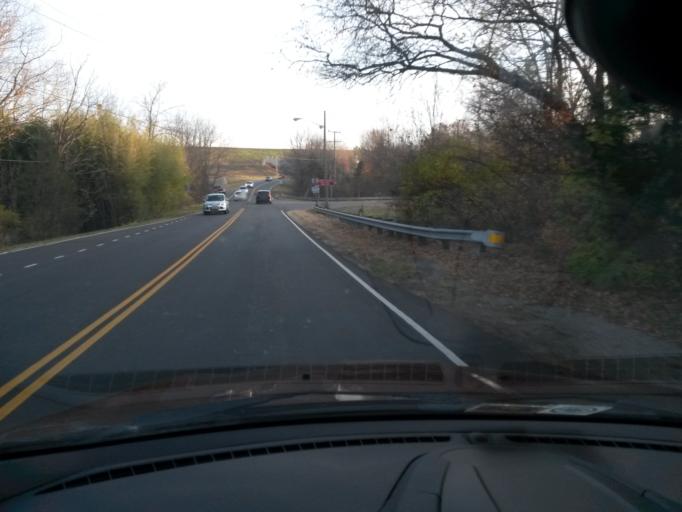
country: US
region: Virginia
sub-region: Roanoke County
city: Hollins
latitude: 37.3372
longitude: -79.9688
